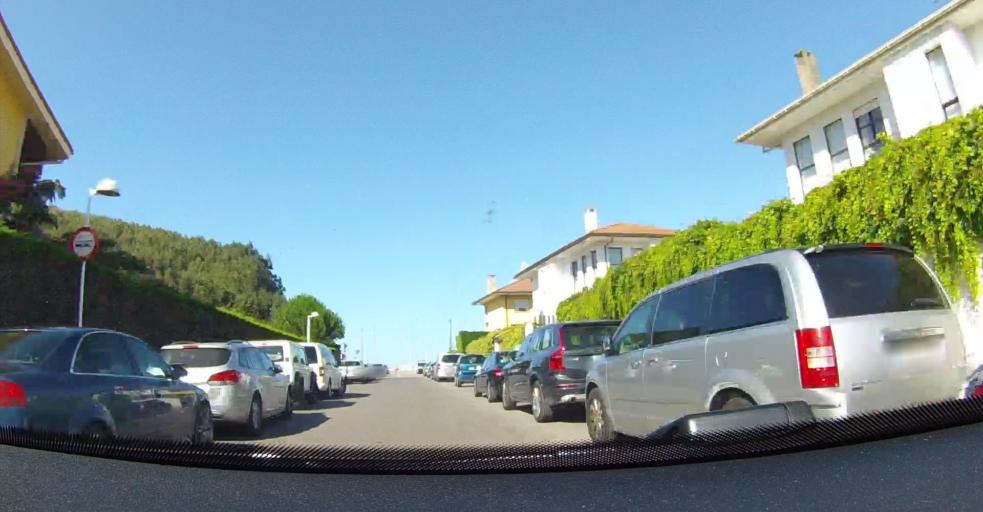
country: ES
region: Asturias
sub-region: Province of Asturias
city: Ribadesella
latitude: 43.4669
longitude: -5.0774
